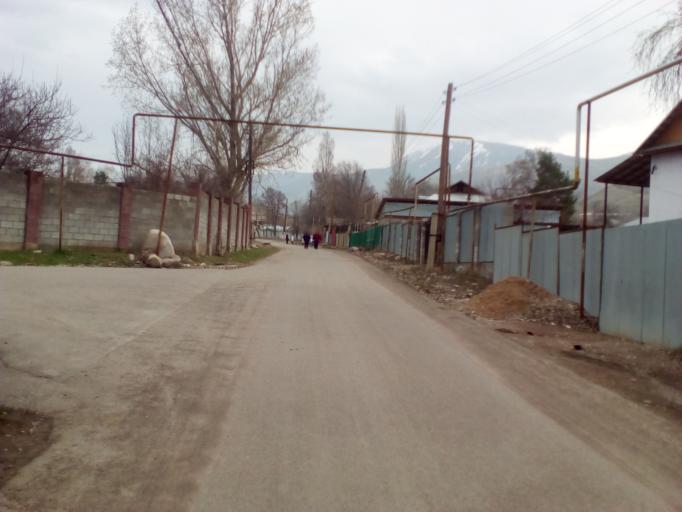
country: KZ
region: Almaty Oblysy
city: Burunday
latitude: 43.1567
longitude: 76.4119
